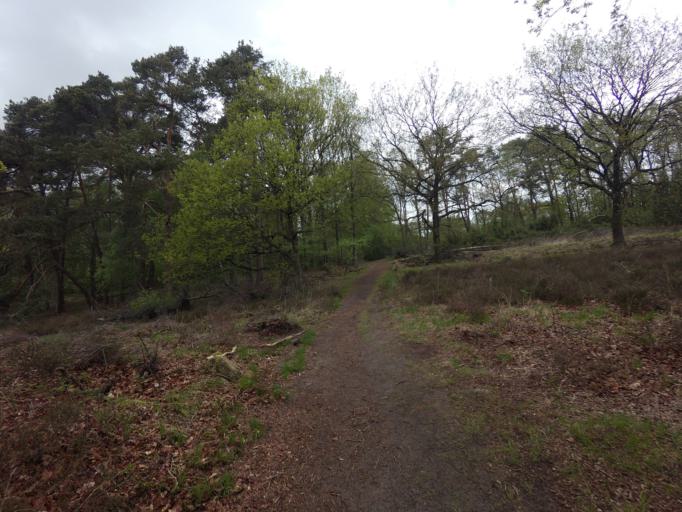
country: NL
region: Overijssel
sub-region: Gemeente Haaksbergen
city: Haaksbergen
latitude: 52.1533
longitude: 6.8072
